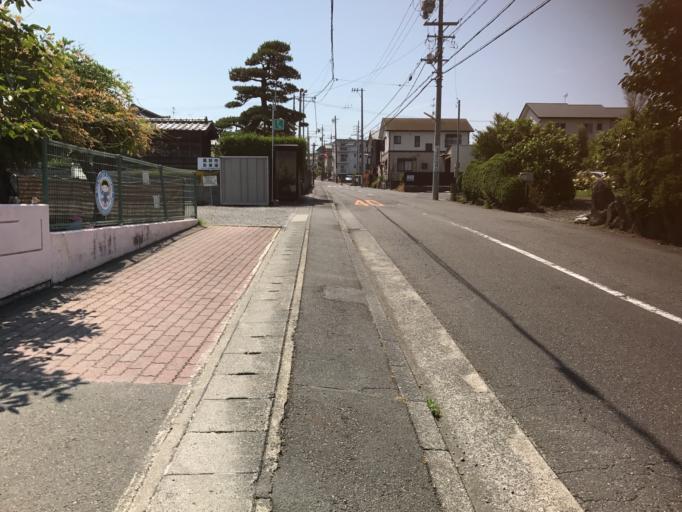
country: JP
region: Shizuoka
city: Shizuoka-shi
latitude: 34.9984
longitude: 138.4405
